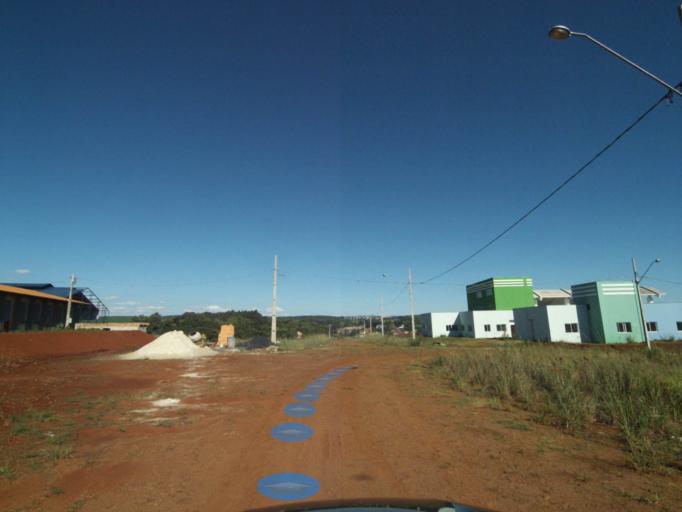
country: BR
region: Parana
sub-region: Coronel Vivida
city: Coronel Vivida
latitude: -26.1395
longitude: -52.3915
